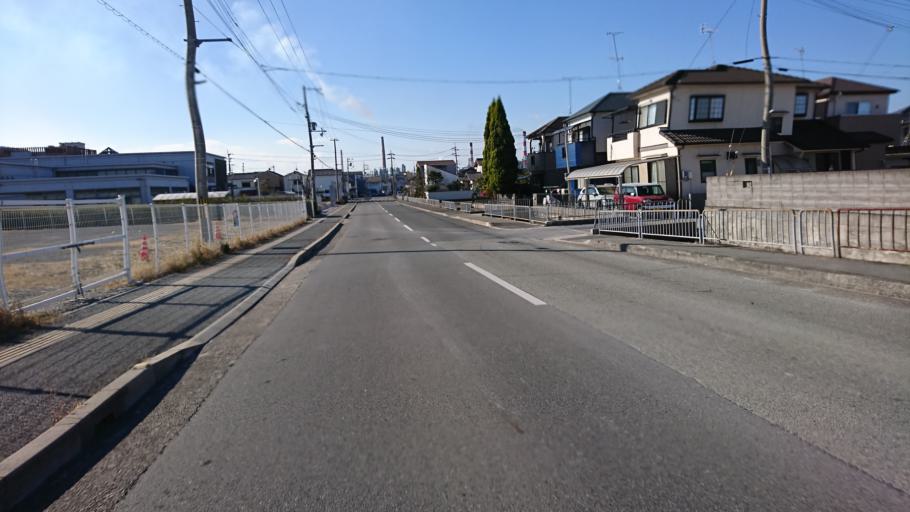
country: JP
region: Hyogo
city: Kakogawacho-honmachi
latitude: 34.7305
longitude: 134.8449
